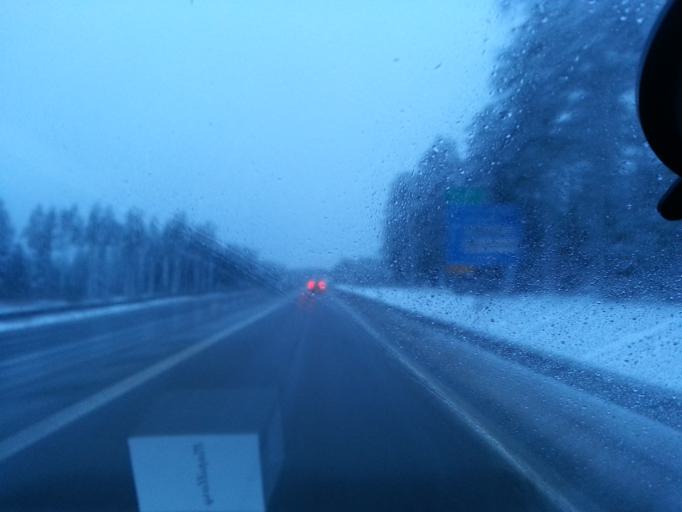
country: SE
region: Kronoberg
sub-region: Ljungby Kommun
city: Lagan
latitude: 56.9488
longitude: 14.0004
